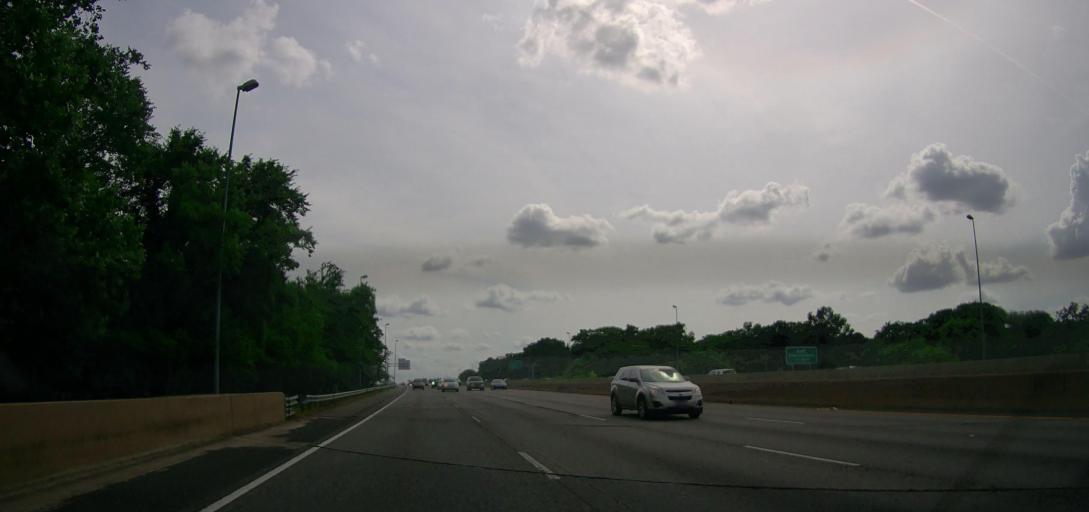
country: US
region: Alabama
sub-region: Jefferson County
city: Birmingham
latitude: 33.5403
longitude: -86.7905
